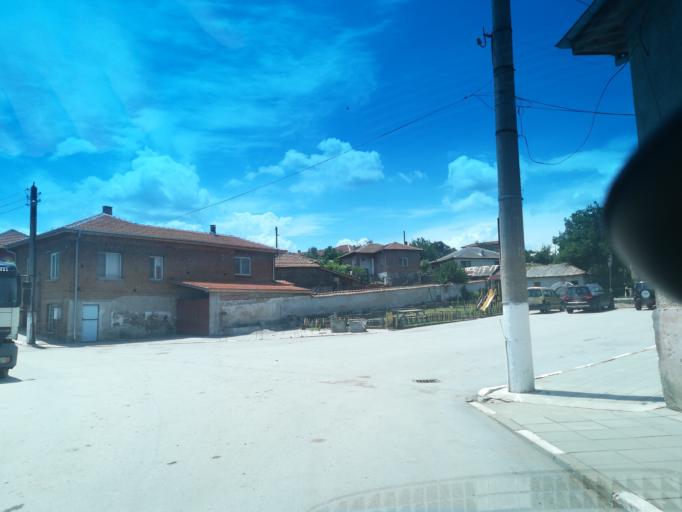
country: BG
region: Khaskovo
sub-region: Obshtina Mineralni Bani
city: Mineralni Bani
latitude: 41.9458
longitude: 25.2442
